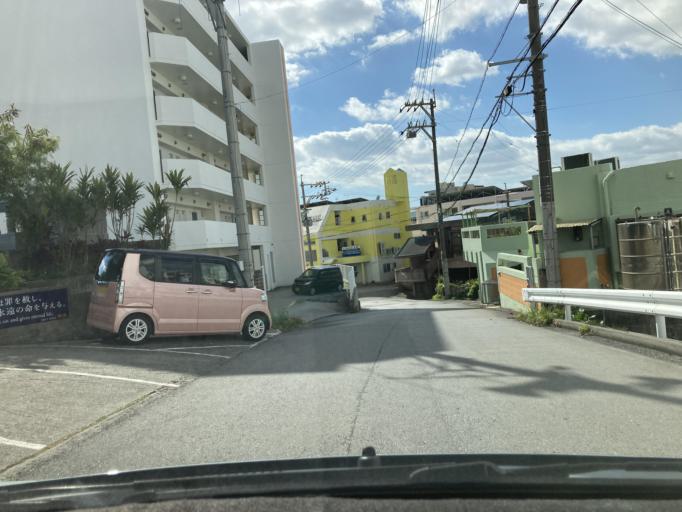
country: JP
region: Okinawa
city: Okinawa
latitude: 26.3281
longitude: 127.8170
